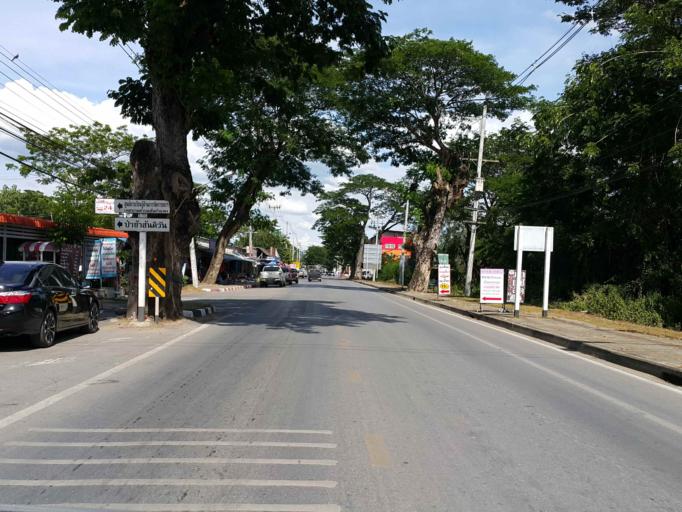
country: TH
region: Chiang Mai
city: San Kamphaeng
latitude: 18.7502
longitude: 99.1099
